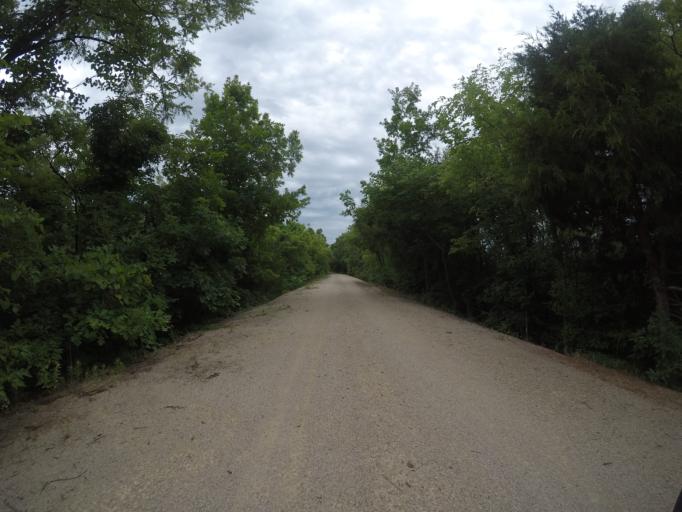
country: US
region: Kansas
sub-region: Anderson County
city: Garnett
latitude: 38.3129
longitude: -95.2491
